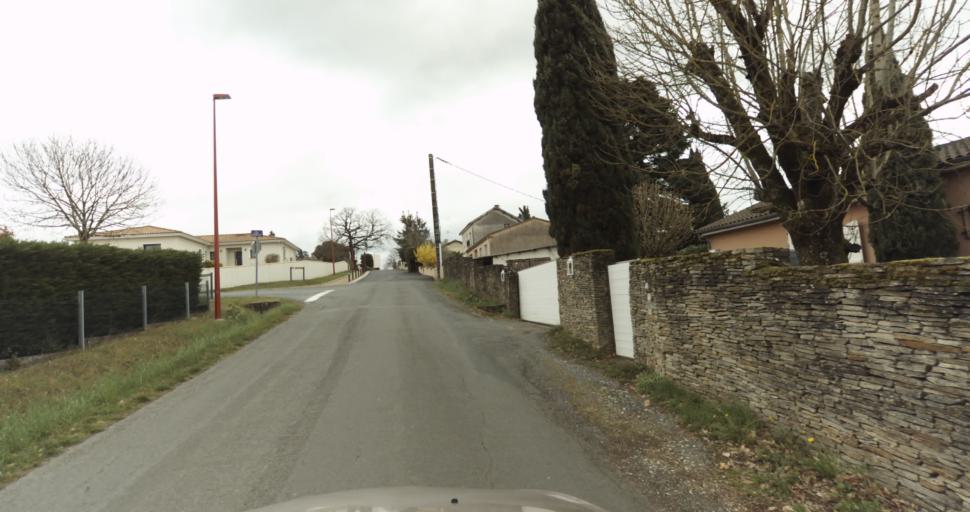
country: FR
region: Midi-Pyrenees
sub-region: Departement du Tarn
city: Puygouzon
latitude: 43.9027
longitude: 2.1621
